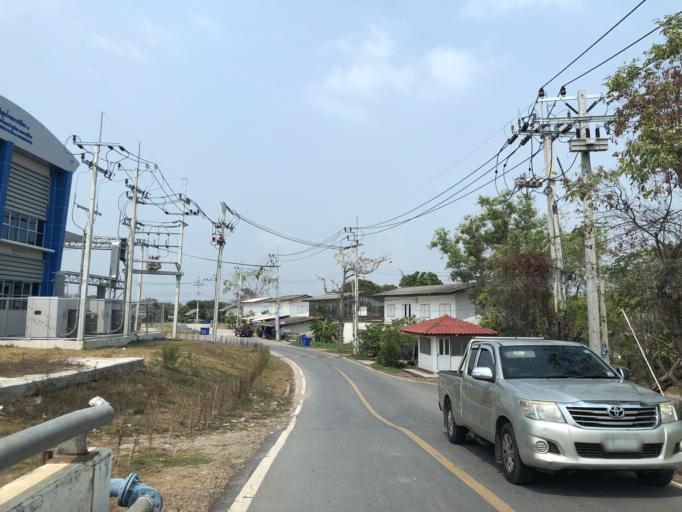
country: TH
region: Samut Prakan
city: Bang Bo
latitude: 13.5178
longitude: 100.8233
